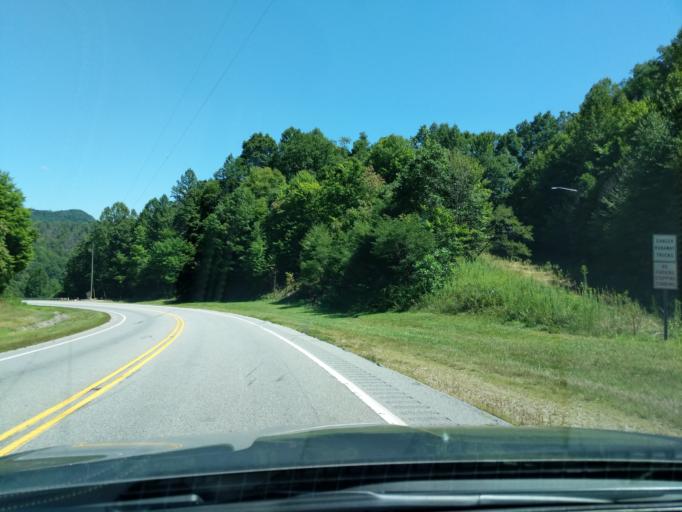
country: US
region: North Carolina
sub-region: Macon County
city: Franklin
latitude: 35.1314
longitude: -83.5150
